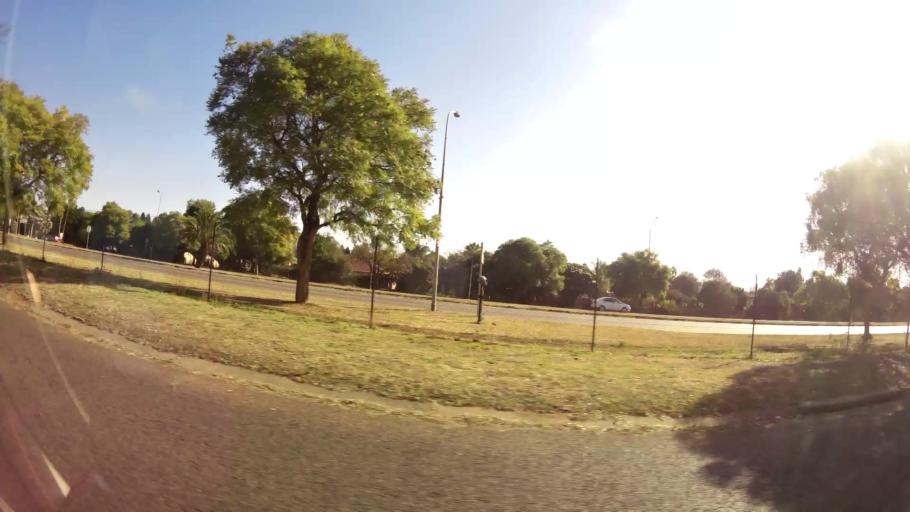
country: ZA
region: Gauteng
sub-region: City of Tshwane Metropolitan Municipality
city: Pretoria
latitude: -25.7270
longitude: 28.2588
